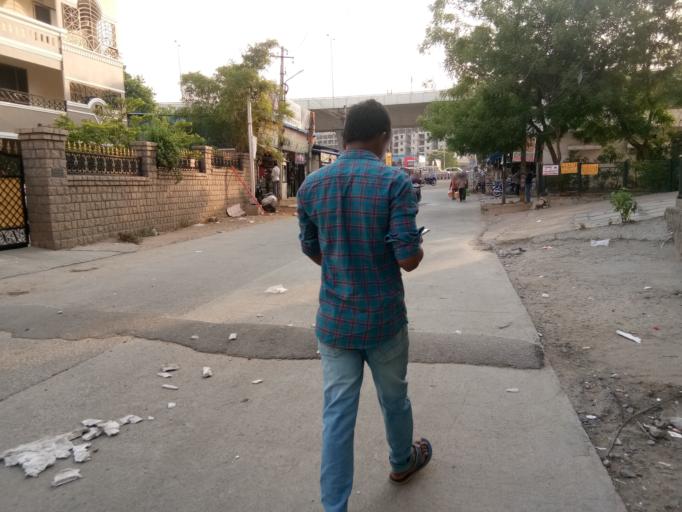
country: IN
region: Telangana
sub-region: Hyderabad
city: Hyderabad
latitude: 17.3290
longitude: 78.4253
